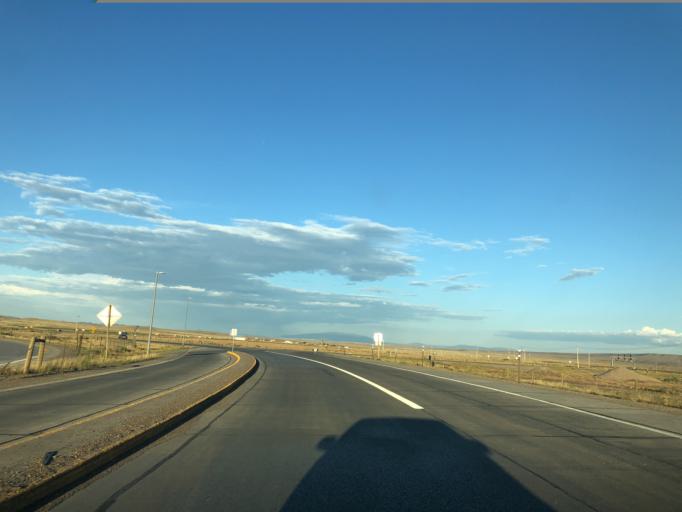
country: US
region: Wyoming
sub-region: Carbon County
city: Rawlins
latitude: 41.7875
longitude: -107.1978
